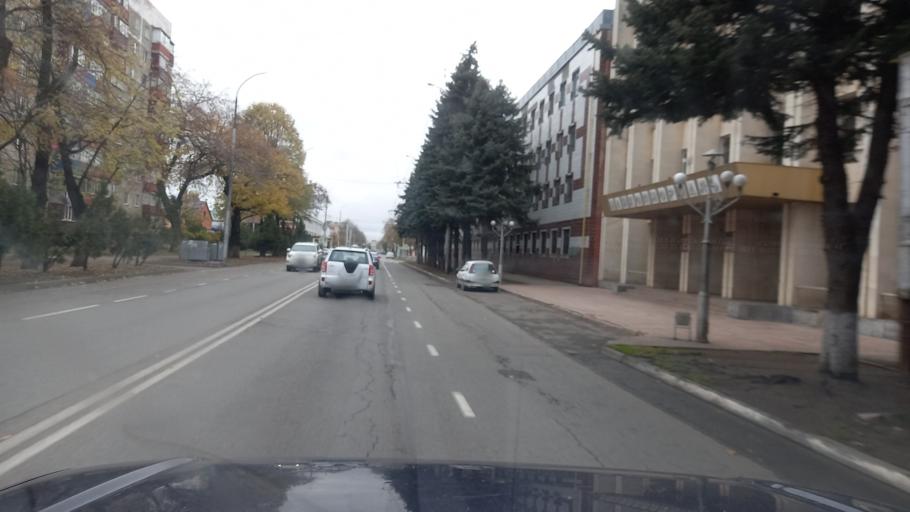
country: RU
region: Adygeya
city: Maykop
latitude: 44.6128
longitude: 40.1083
